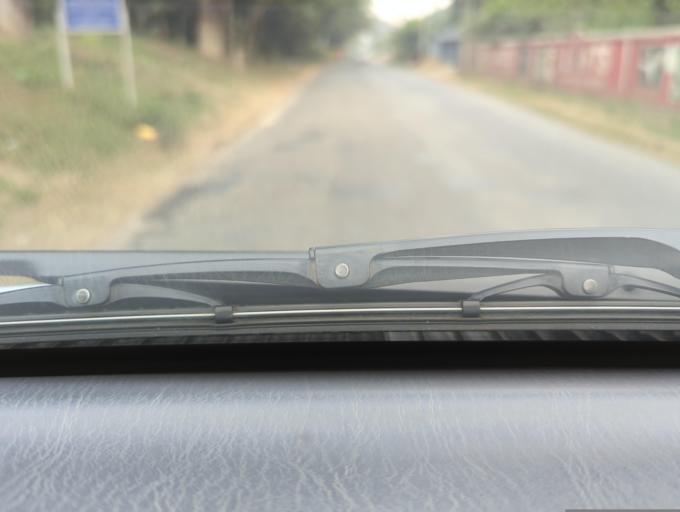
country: BD
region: Sylhet
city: Maulavi Bazar
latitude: 24.5083
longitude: 91.7303
